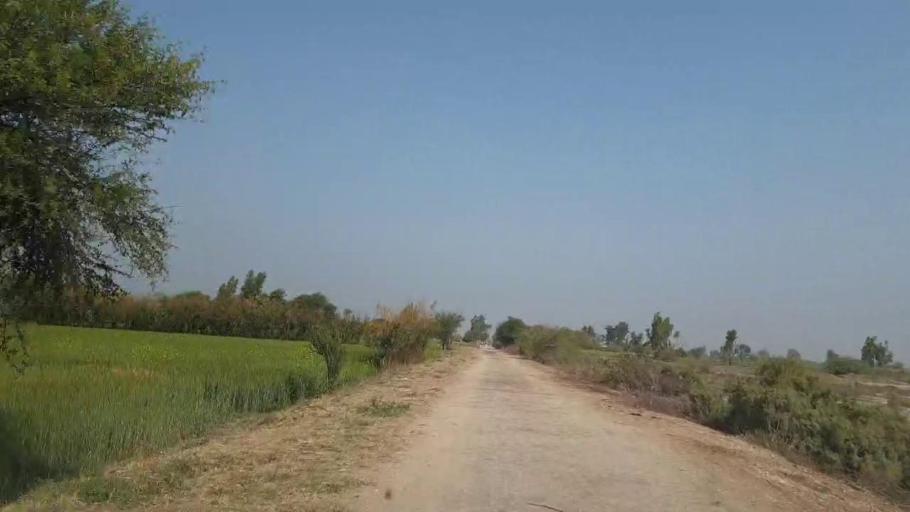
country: PK
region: Sindh
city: Mirpur Khas
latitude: 25.5876
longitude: 69.0150
